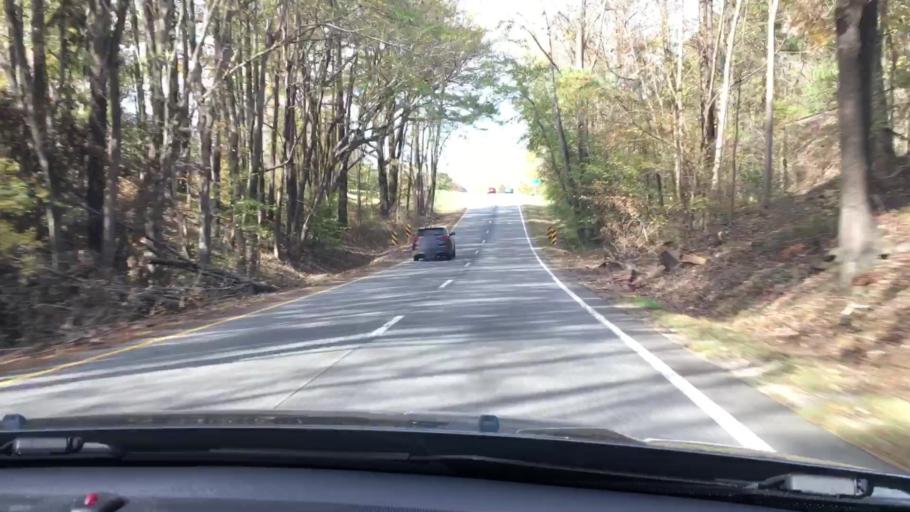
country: US
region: Virginia
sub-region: James City County
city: Williamsburg
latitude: 37.3263
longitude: -76.7393
